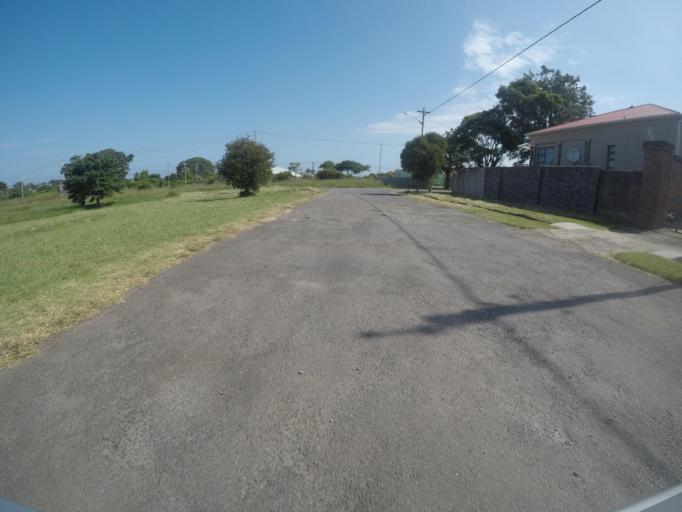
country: ZA
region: Eastern Cape
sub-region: Buffalo City Metropolitan Municipality
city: East London
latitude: -32.9700
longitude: 27.8757
